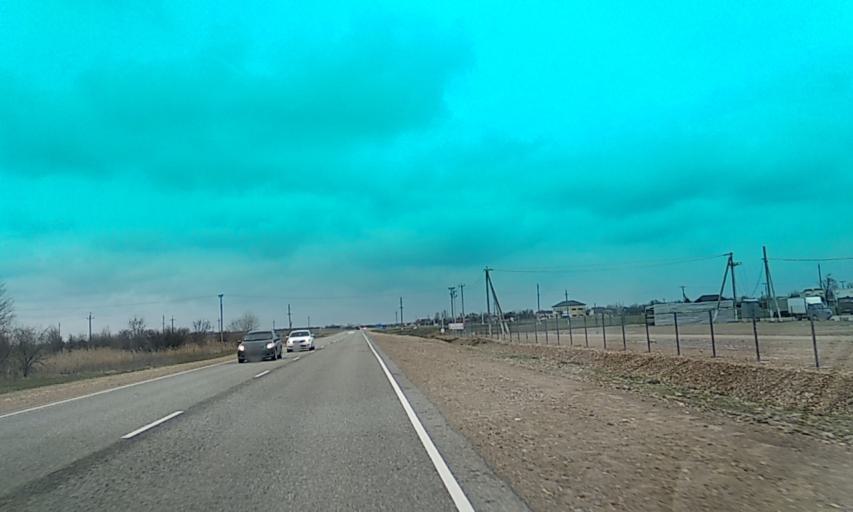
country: RU
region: Krasnodarskiy
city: Velikovechnoye
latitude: 44.9320
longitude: 39.7769
